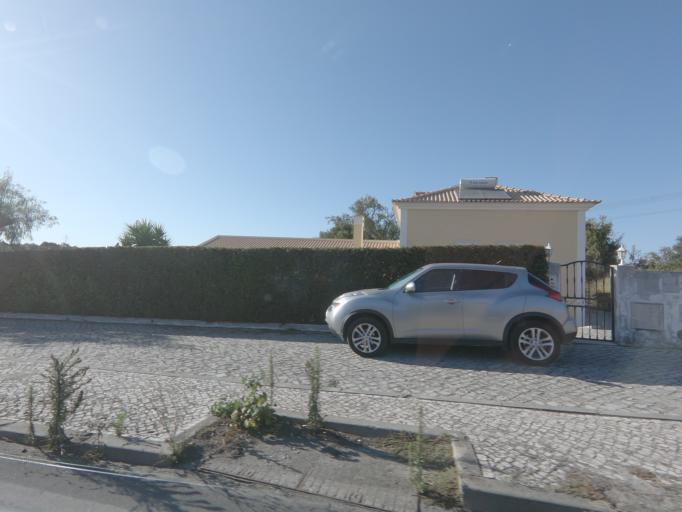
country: PT
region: Setubal
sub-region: Palmela
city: Palmela
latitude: 38.5675
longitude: -8.9188
